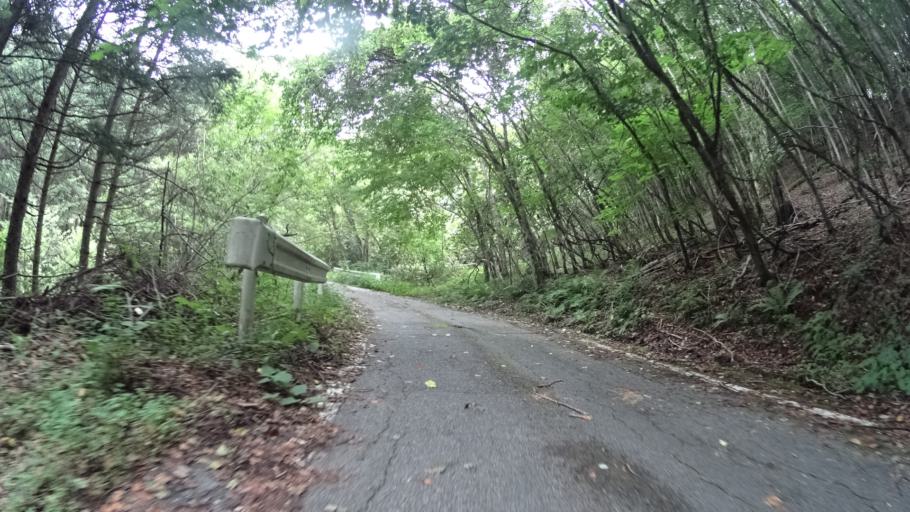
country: JP
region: Yamanashi
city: Enzan
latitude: 35.8089
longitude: 138.6288
